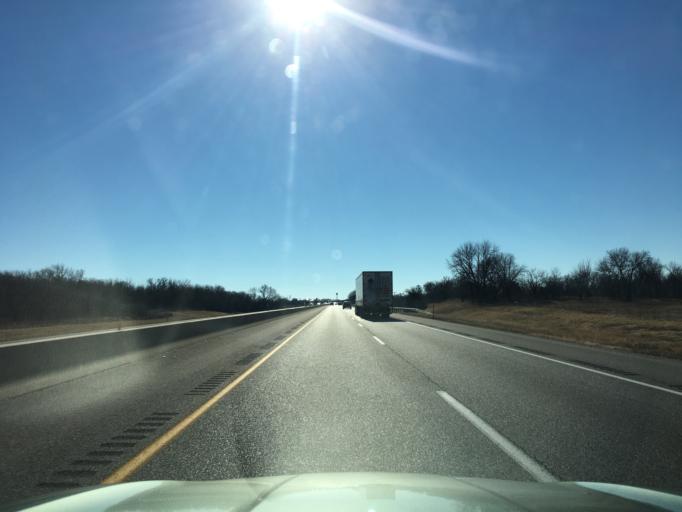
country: US
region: Kansas
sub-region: Sumner County
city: Belle Plaine
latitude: 37.3868
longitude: -97.3249
